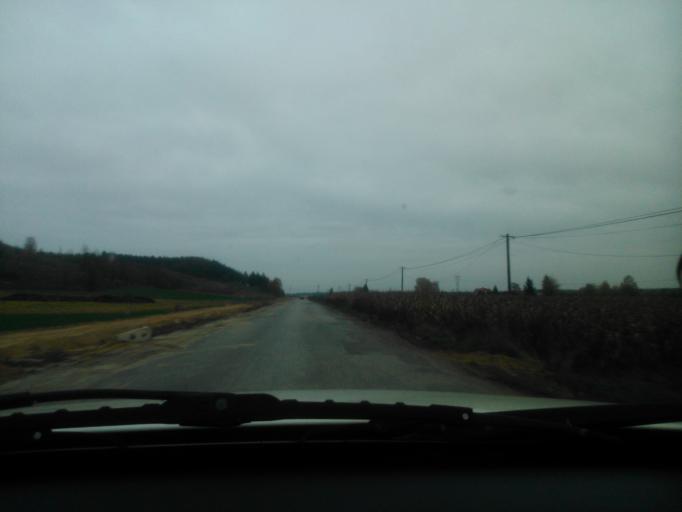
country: PL
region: Kujawsko-Pomorskie
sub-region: Powiat golubsko-dobrzynski
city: Golub-Dobrzyn
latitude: 53.1261
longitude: 19.0797
